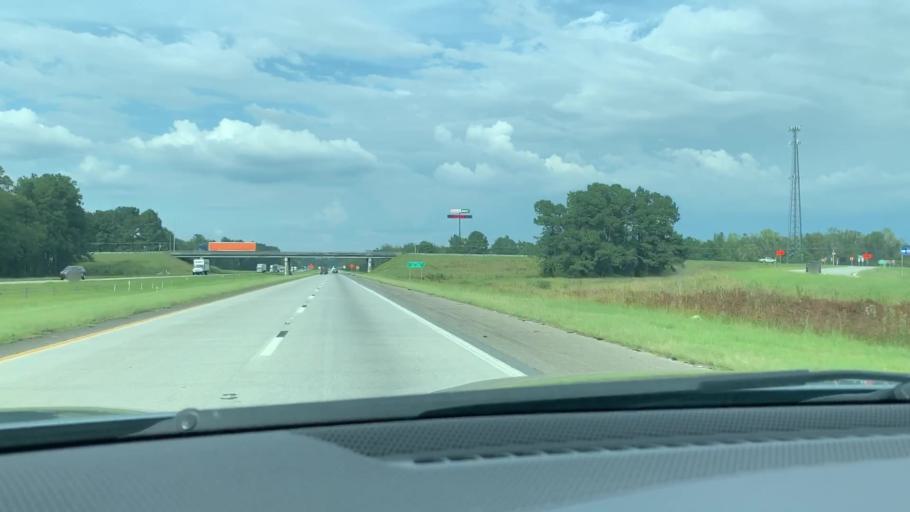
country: US
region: South Carolina
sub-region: Dorchester County
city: Saint George
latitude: 33.0822
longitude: -80.6537
